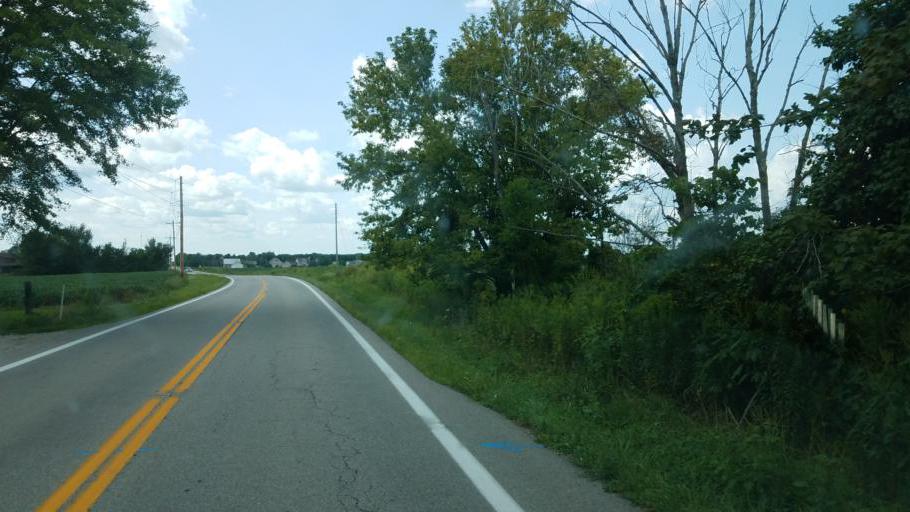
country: US
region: Ohio
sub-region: Delaware County
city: Sunbury
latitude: 40.3242
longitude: -82.8742
